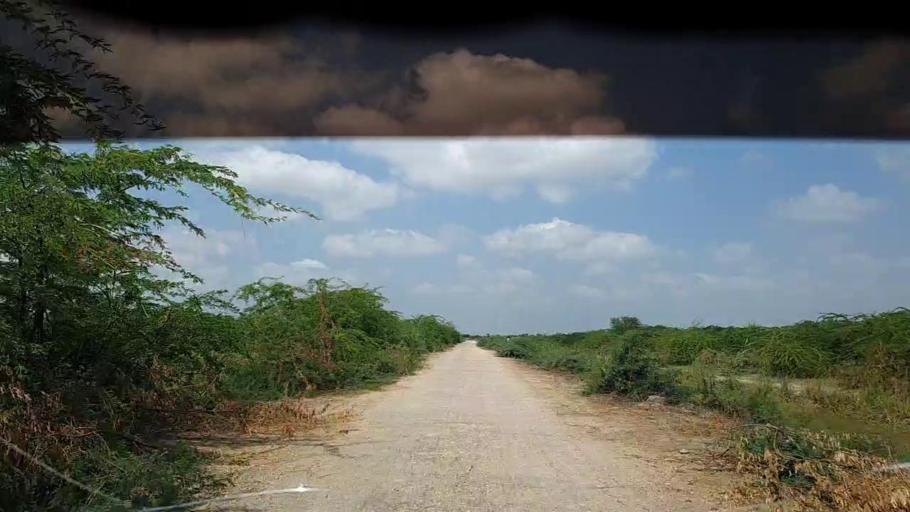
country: PK
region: Sindh
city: Kadhan
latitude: 24.5859
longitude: 68.9698
